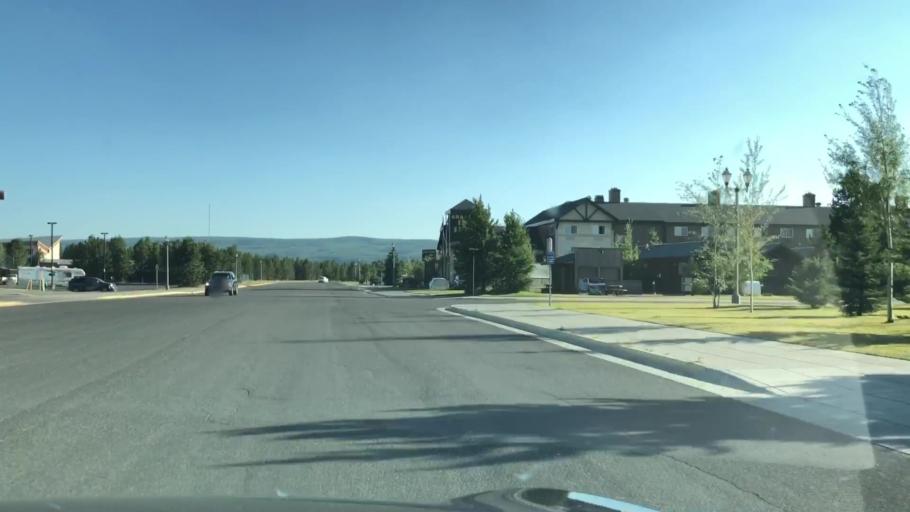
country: US
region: Montana
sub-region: Gallatin County
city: West Yellowstone
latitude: 44.6568
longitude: -111.0997
